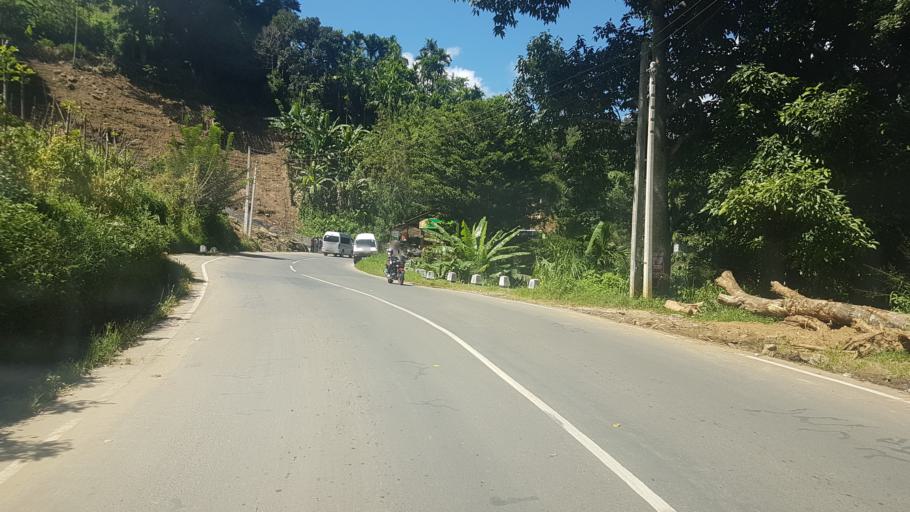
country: LK
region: Uva
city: Badulla
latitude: 6.8662
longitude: 81.0515
